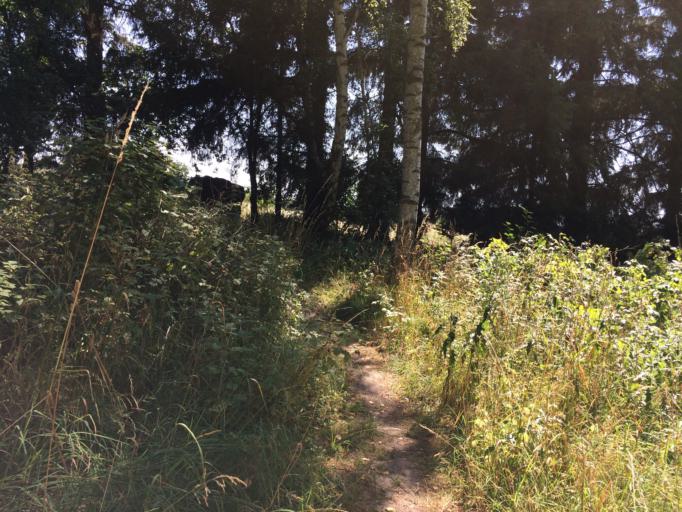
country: DK
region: Capital Region
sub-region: Fureso Kommune
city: Stavnsholt
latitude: 55.8312
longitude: 12.3981
